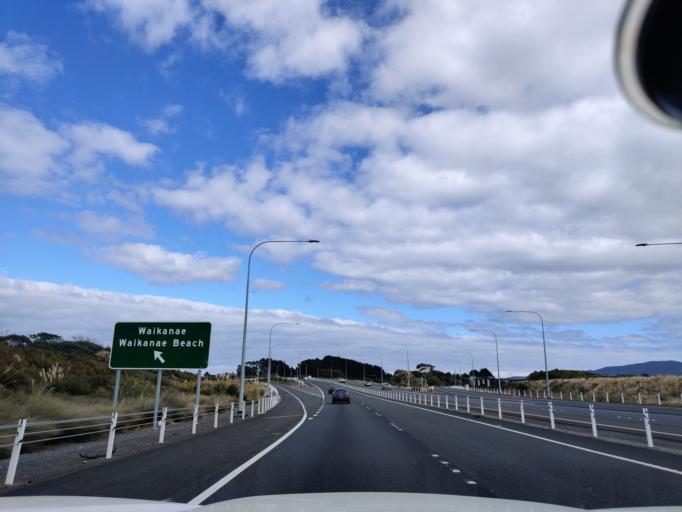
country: NZ
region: Wellington
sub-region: Kapiti Coast District
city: Paraparaumu
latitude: -40.8663
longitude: 175.0401
